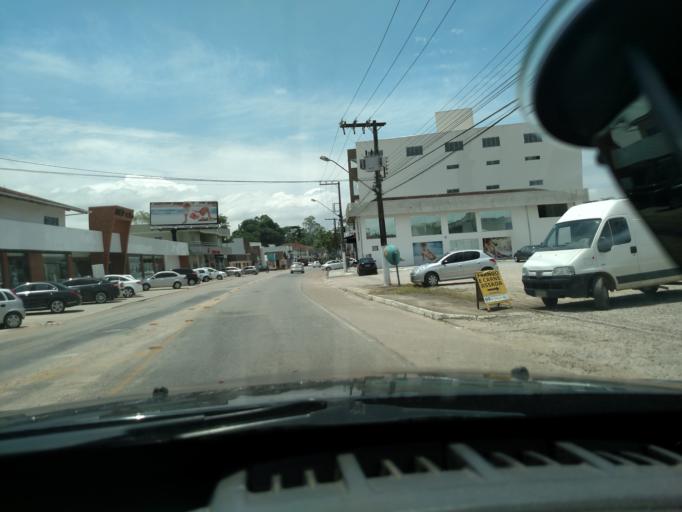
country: BR
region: Santa Catarina
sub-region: Gaspar
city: Gaspar
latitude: -26.9044
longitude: -48.8376
